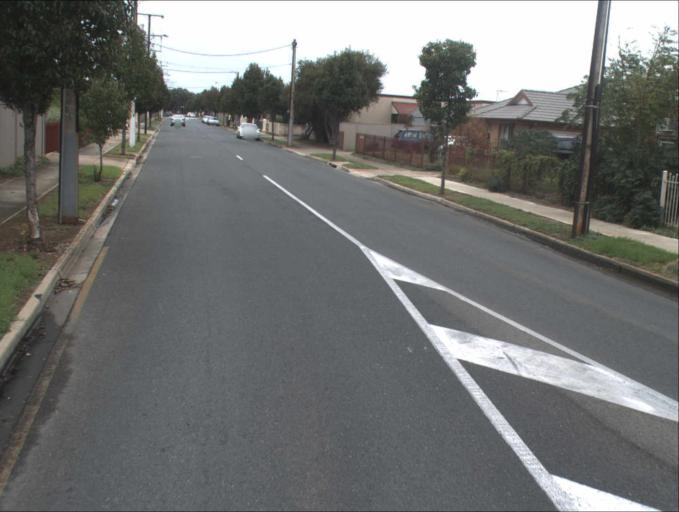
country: AU
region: South Australia
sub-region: Charles Sturt
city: Woodville North
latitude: -34.8683
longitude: 138.5562
